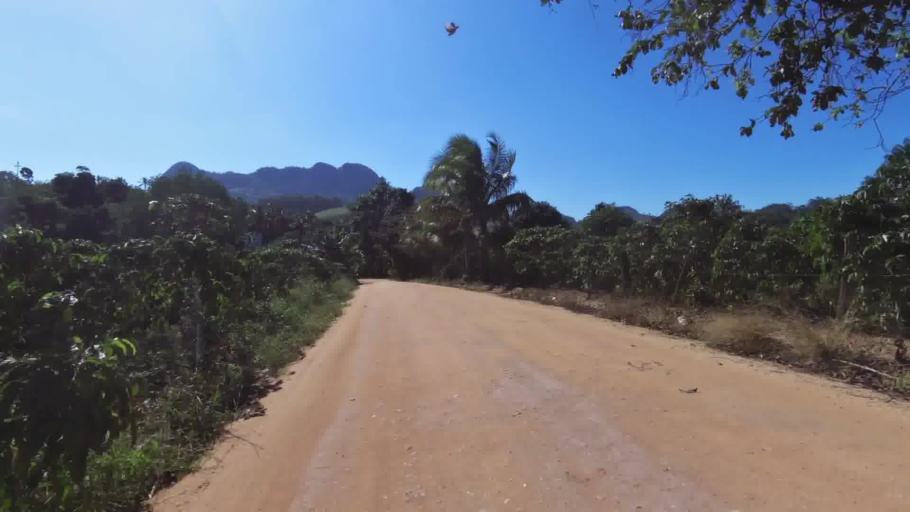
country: BR
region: Espirito Santo
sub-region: Iconha
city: Iconha
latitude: -20.8161
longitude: -40.8402
